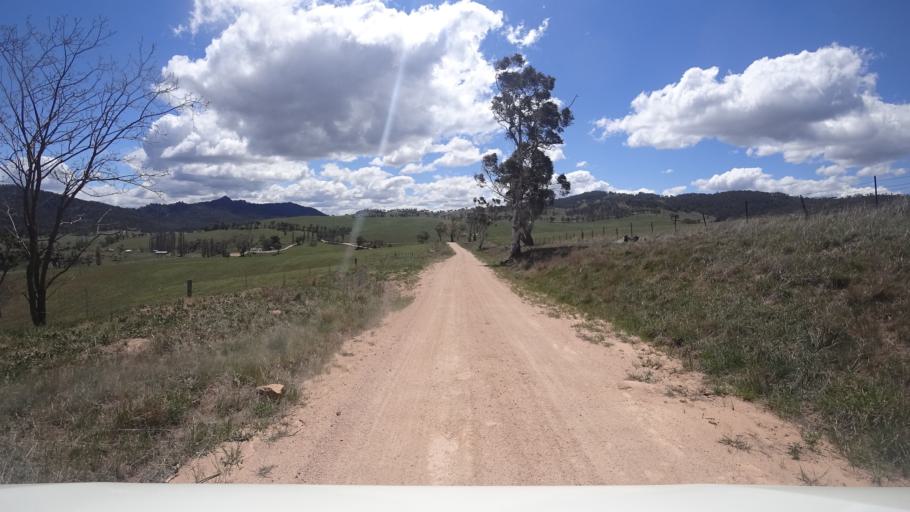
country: AU
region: New South Wales
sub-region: Oberon
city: Oberon
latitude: -33.5703
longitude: 149.9421
